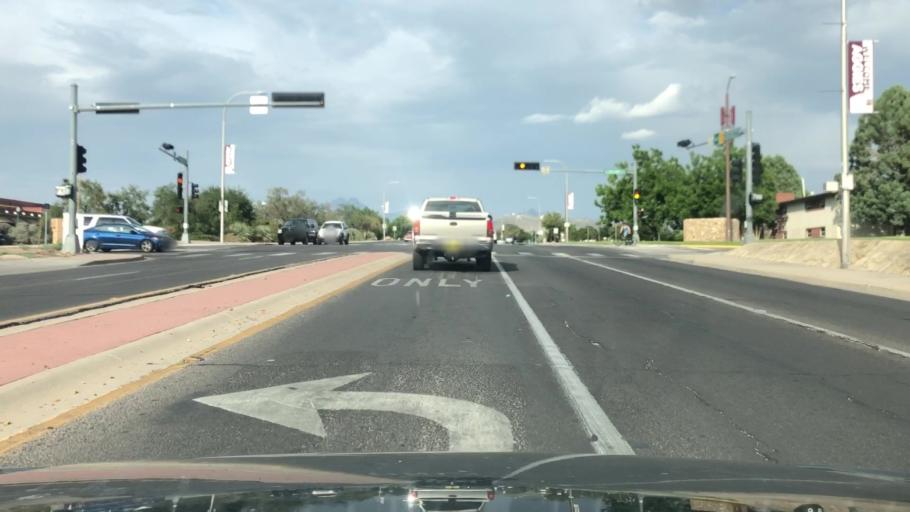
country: US
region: New Mexico
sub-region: Dona Ana County
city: University Park
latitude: 32.2857
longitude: -106.7479
